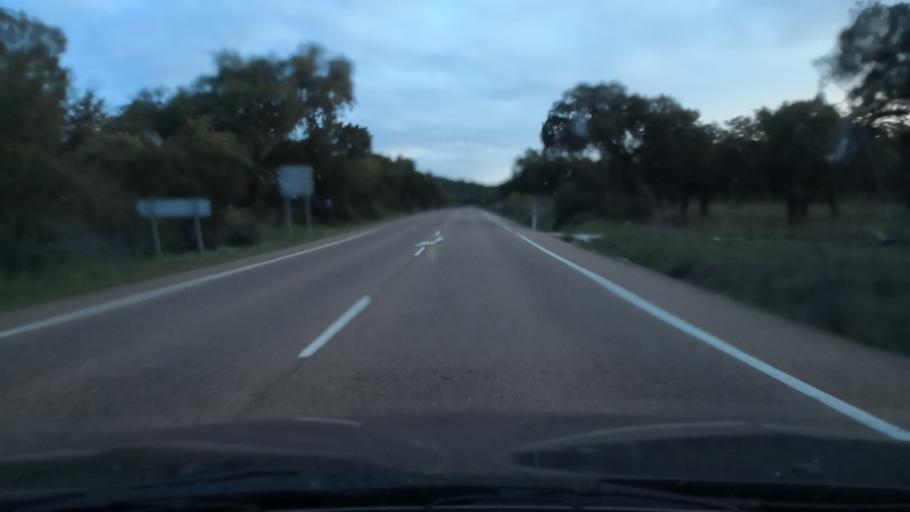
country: ES
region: Extremadura
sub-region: Provincia de Badajoz
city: Puebla de Obando
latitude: 39.1952
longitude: -6.5948
